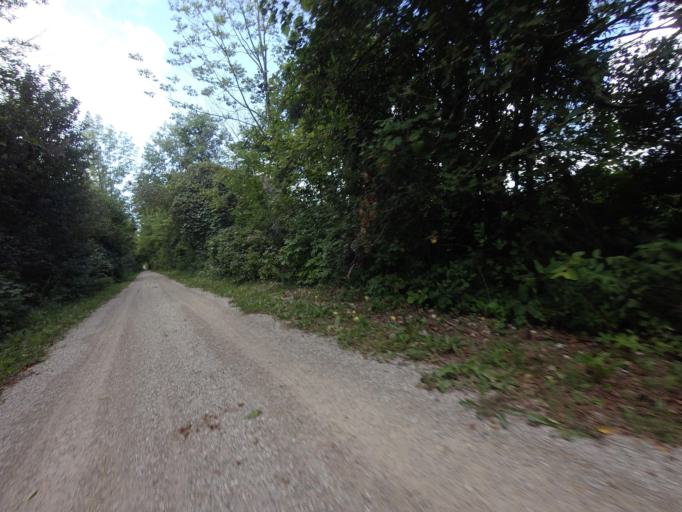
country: CA
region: Ontario
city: Huron East
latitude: 43.7385
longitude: -81.4660
